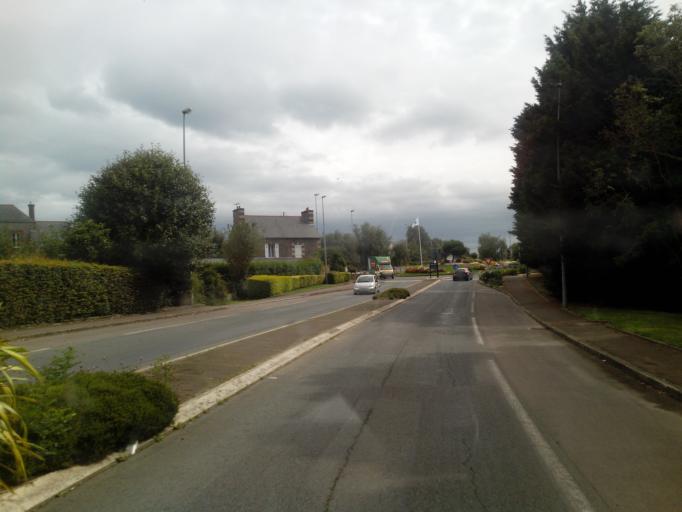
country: FR
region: Brittany
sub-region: Departement des Cotes-d'Armor
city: Saint-Quay-Portrieux
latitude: 48.6493
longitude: -2.8392
